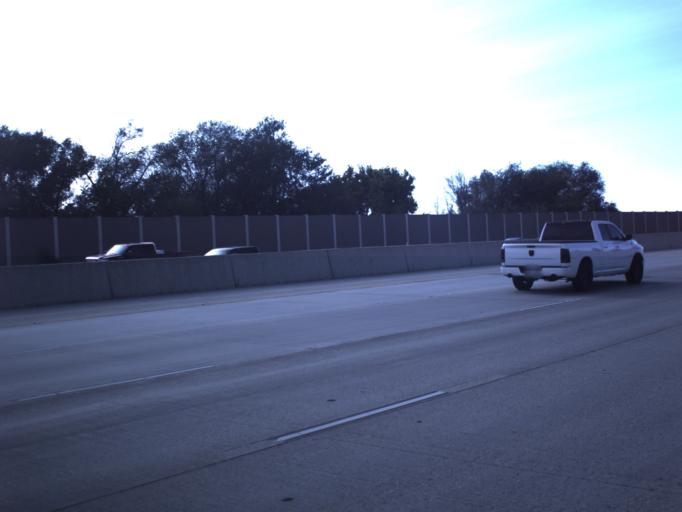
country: US
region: Utah
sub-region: Salt Lake County
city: Taylorsville
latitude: 40.6500
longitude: -111.9513
